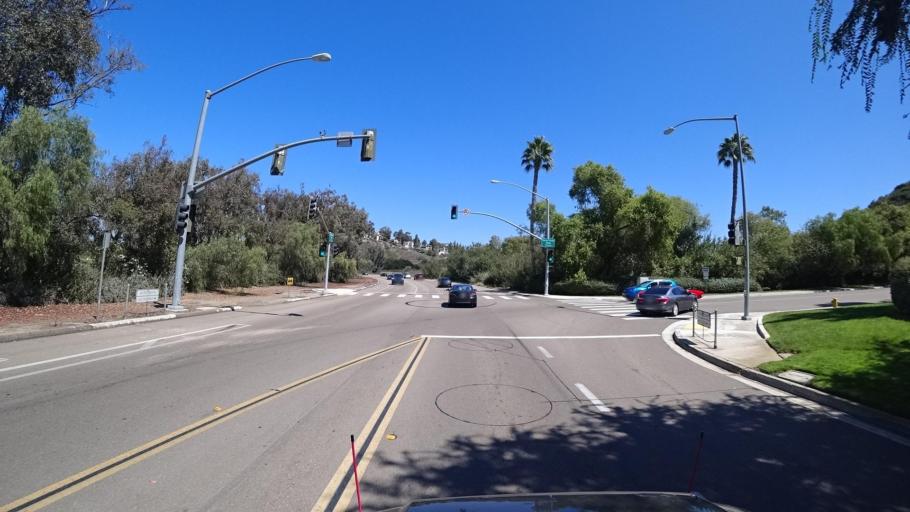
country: US
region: California
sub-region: San Diego County
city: Fairbanks Ranch
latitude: 32.9789
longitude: -117.2070
